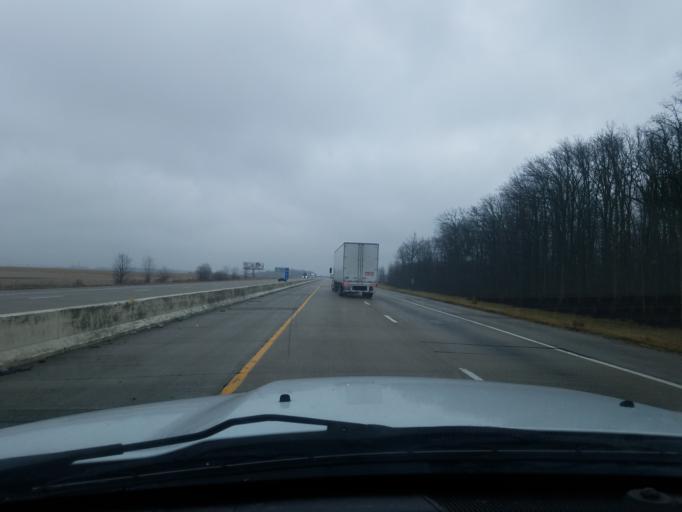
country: US
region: Indiana
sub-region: Wells County
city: Ossian
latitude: 40.9521
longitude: -85.2378
